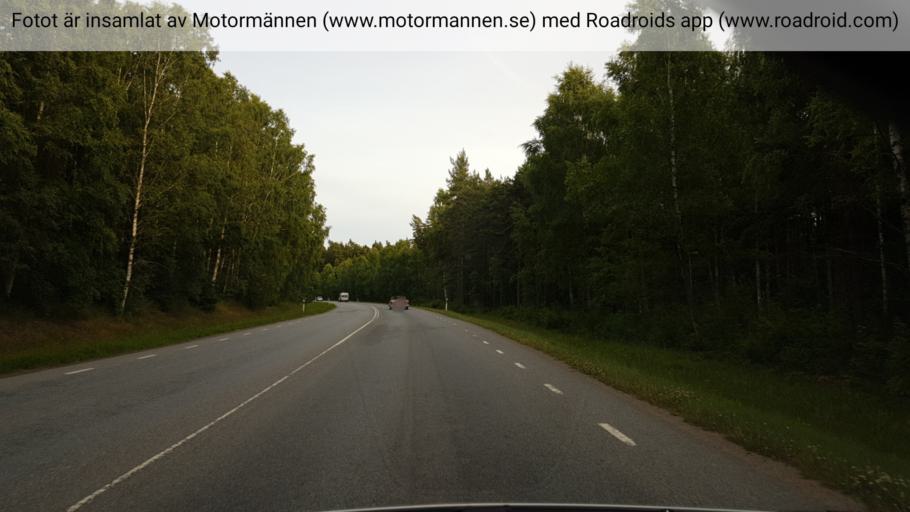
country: SE
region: Vaestra Goetaland
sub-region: Lidkopings Kommun
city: Lidkoping
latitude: 58.4972
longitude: 13.1312
